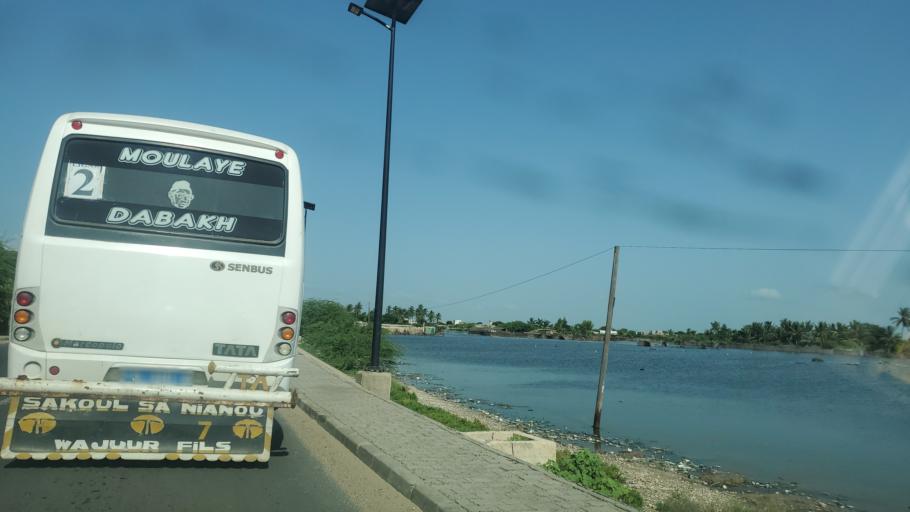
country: SN
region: Saint-Louis
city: Saint-Louis
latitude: 16.0361
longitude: -16.4662
